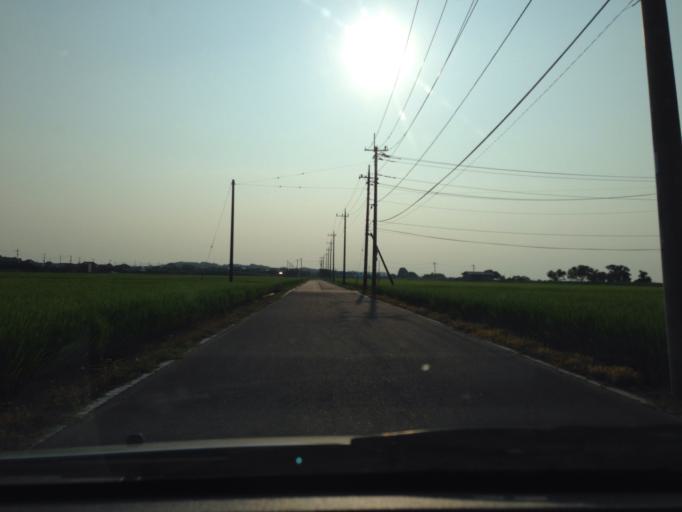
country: JP
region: Ibaraki
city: Inashiki
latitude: 36.0257
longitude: 140.3038
